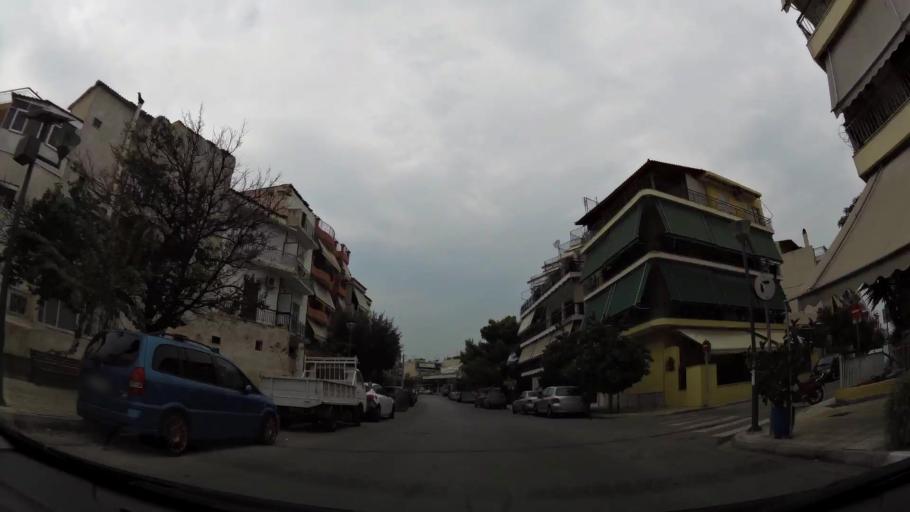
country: GR
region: Attica
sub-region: Nomarchia Athinas
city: Aigaleo
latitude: 37.9848
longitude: 23.6753
